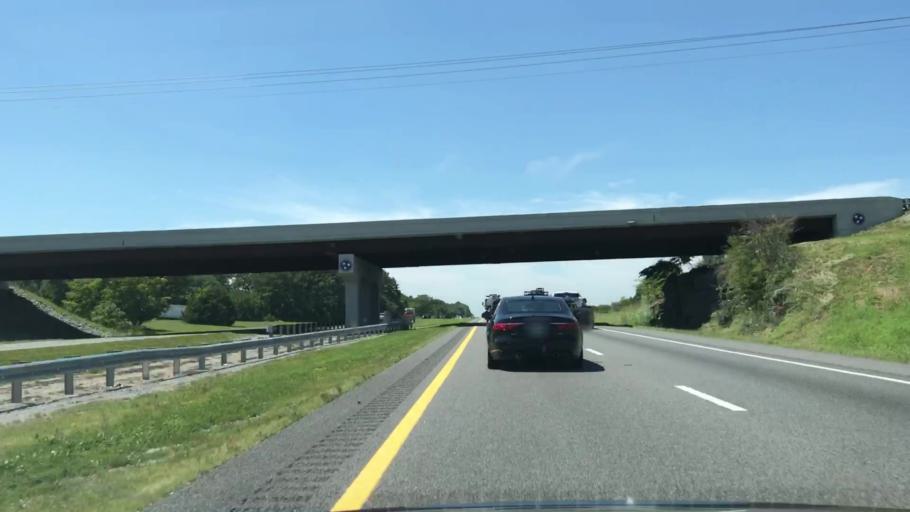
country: US
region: Tennessee
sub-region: Wilson County
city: Watertown
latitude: 36.1908
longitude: -86.1766
